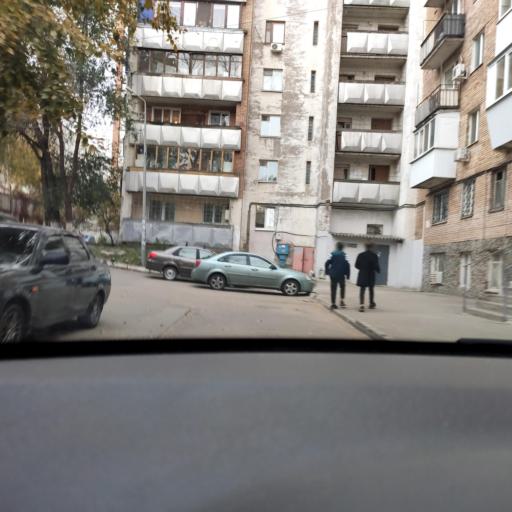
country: RU
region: Samara
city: Samara
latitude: 53.2171
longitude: 50.1511
